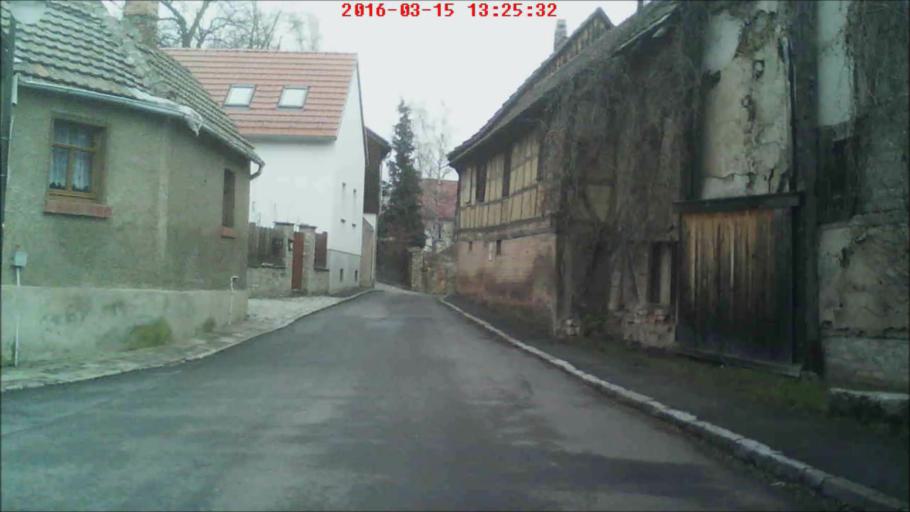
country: DE
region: Thuringia
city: Ingersleben
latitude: 50.9342
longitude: 10.9908
